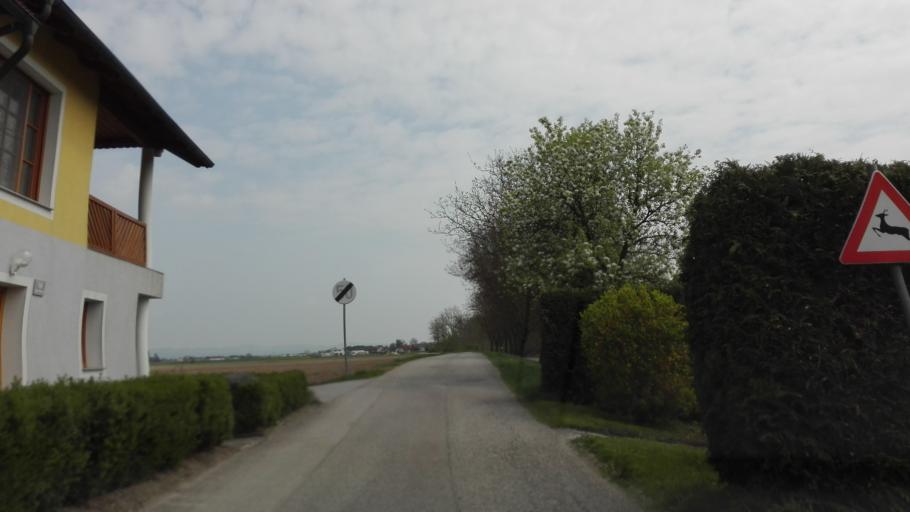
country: AT
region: Lower Austria
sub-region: Politischer Bezirk Amstetten
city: Strengberg
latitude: 48.1823
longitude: 14.6558
